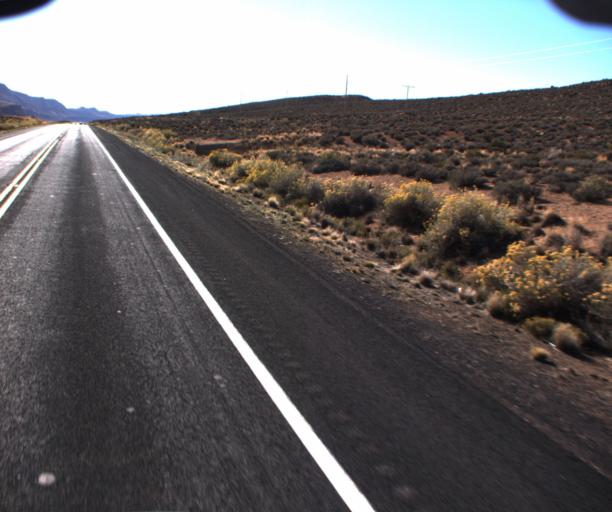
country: US
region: Arizona
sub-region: Coconino County
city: Tuba City
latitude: 36.2663
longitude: -111.4303
